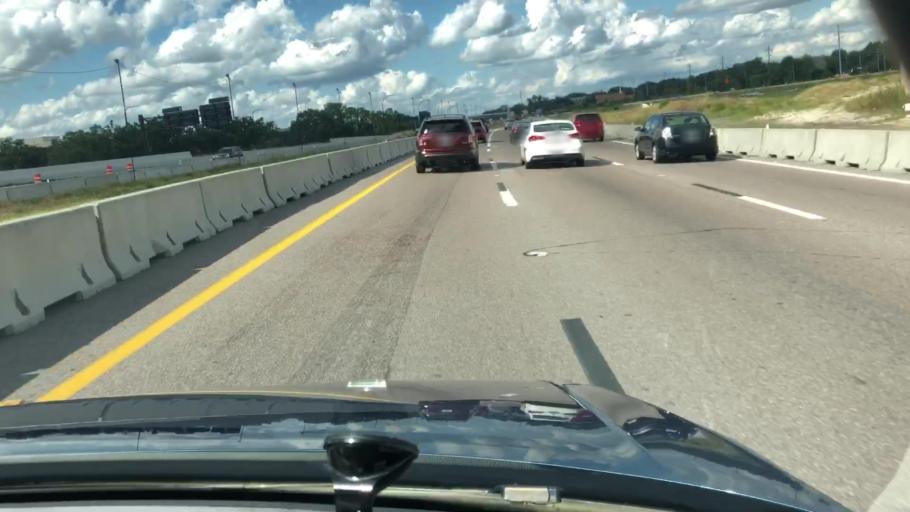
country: US
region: Florida
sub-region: Orange County
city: Eatonville
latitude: 28.6317
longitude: -81.3875
